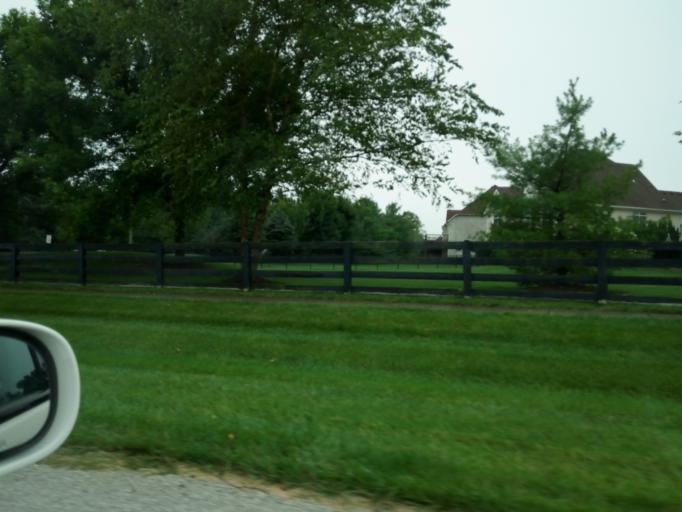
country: US
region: Kentucky
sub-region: Oldham County
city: Pewee Valley
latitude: 38.2715
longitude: -85.4844
